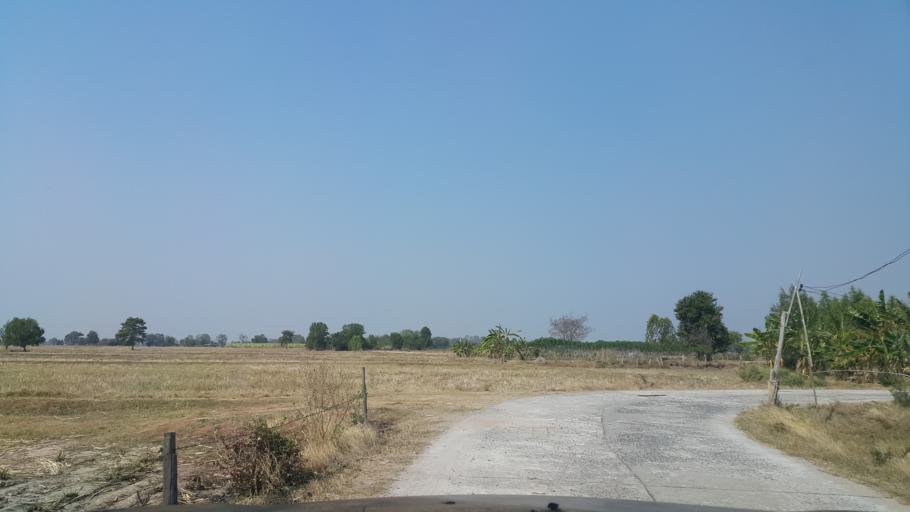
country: TH
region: Buriram
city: Krasang
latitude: 15.0901
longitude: 103.3852
